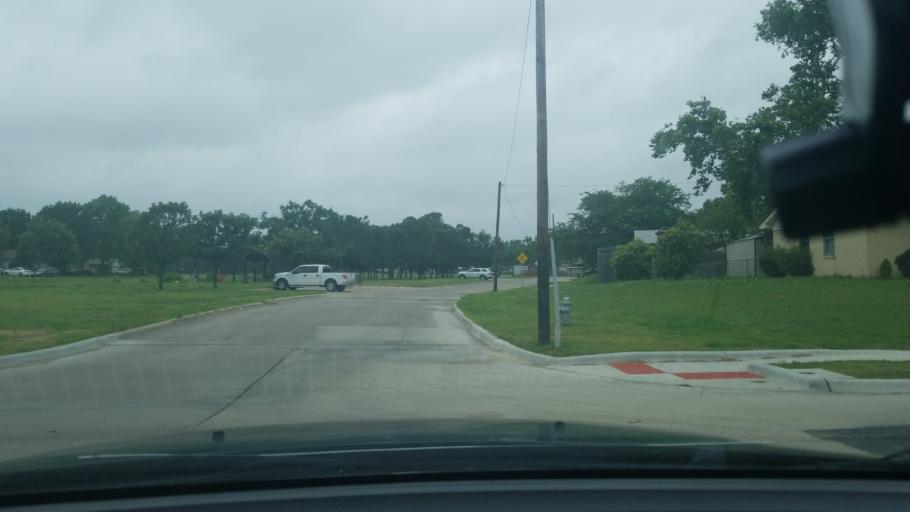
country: US
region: Texas
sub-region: Dallas County
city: Mesquite
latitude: 32.7873
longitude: -96.6345
